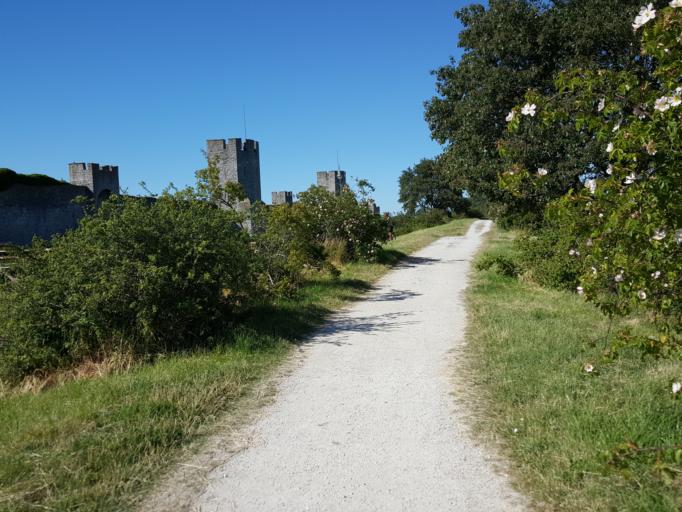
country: SE
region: Gotland
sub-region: Gotland
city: Visby
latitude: 57.6411
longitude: 18.3011
